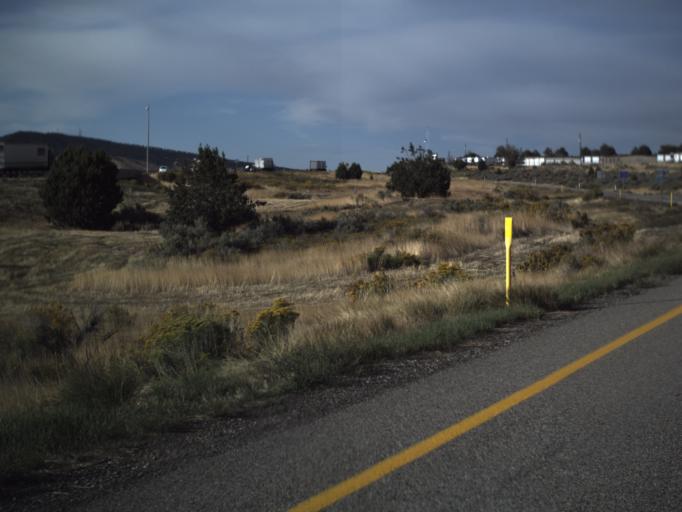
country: US
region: Utah
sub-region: Washington County
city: Toquerville
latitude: 37.4800
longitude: -113.2205
